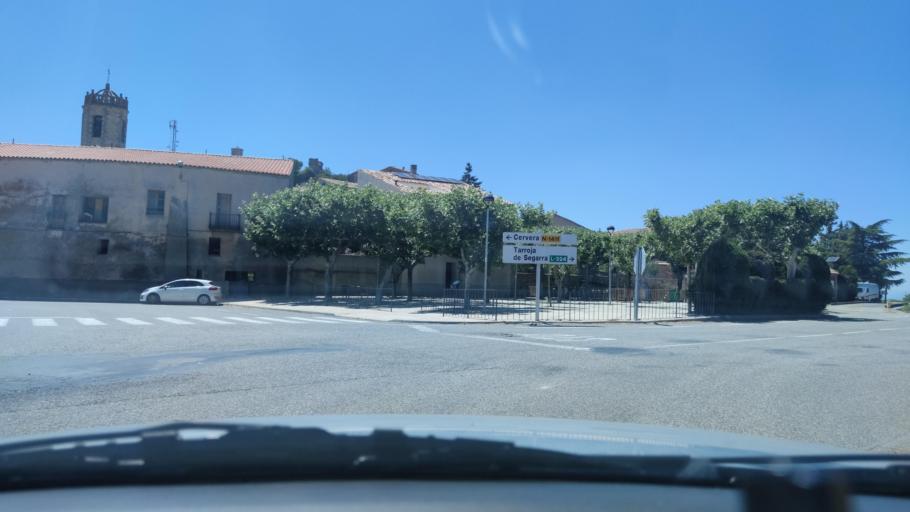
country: ES
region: Catalonia
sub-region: Provincia de Lleida
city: Ivorra
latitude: 41.7248
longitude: 1.3592
